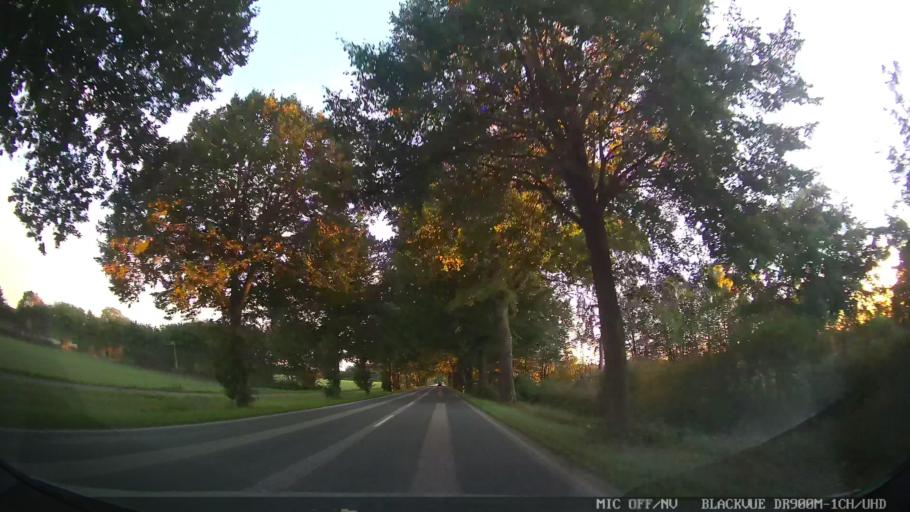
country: DE
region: Schleswig-Holstein
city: Susel
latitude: 54.0658
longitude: 10.6874
